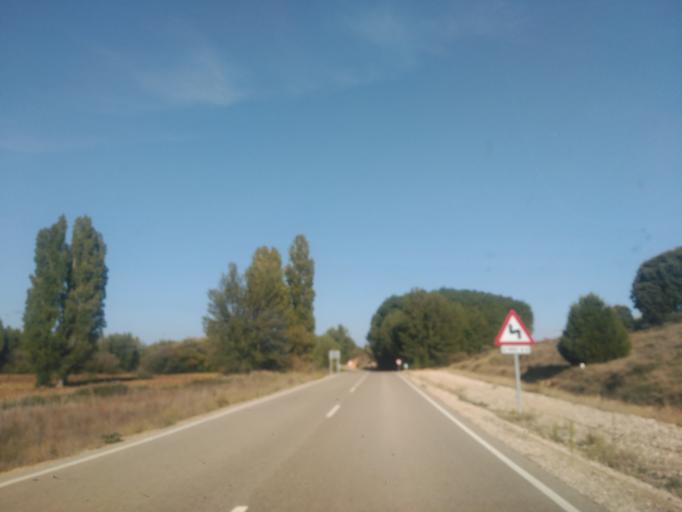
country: ES
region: Castille and Leon
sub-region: Provincia de Soria
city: Alcubilla de Avellaneda
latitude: 41.7544
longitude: -3.2707
